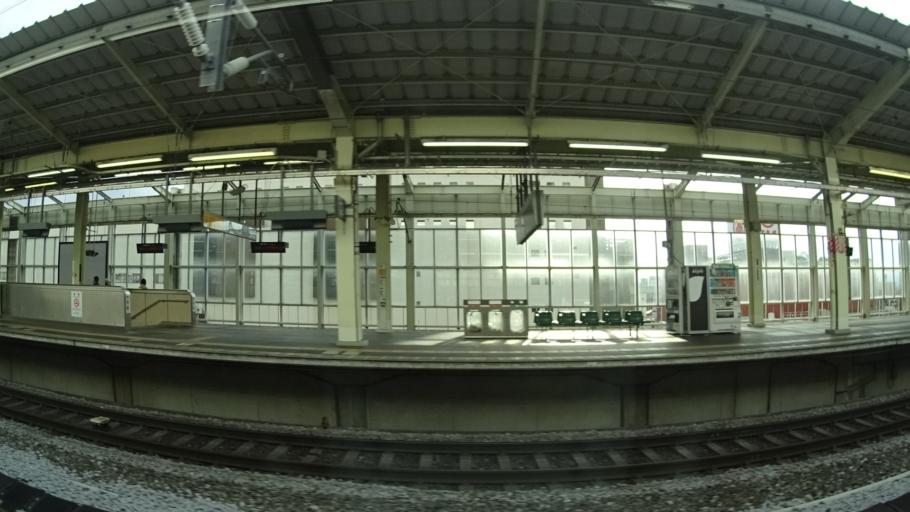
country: JP
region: Gunma
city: Takasaki
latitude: 36.3239
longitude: 139.0128
